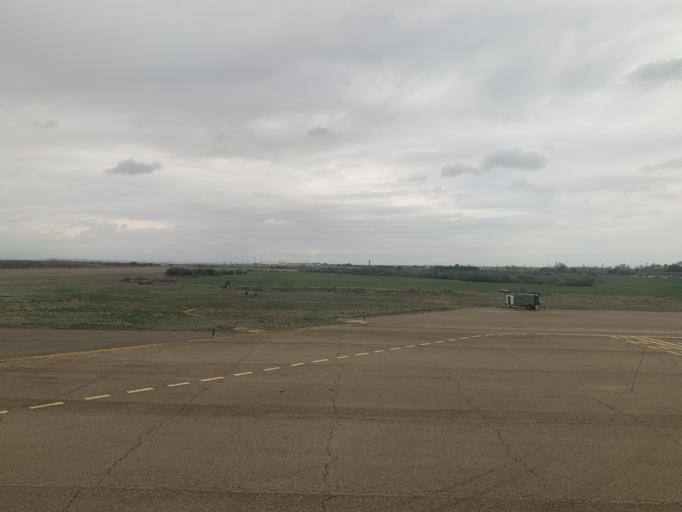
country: ES
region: Aragon
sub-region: Provincia de Zaragoza
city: Utebo
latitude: 41.6699
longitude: -1.0391
